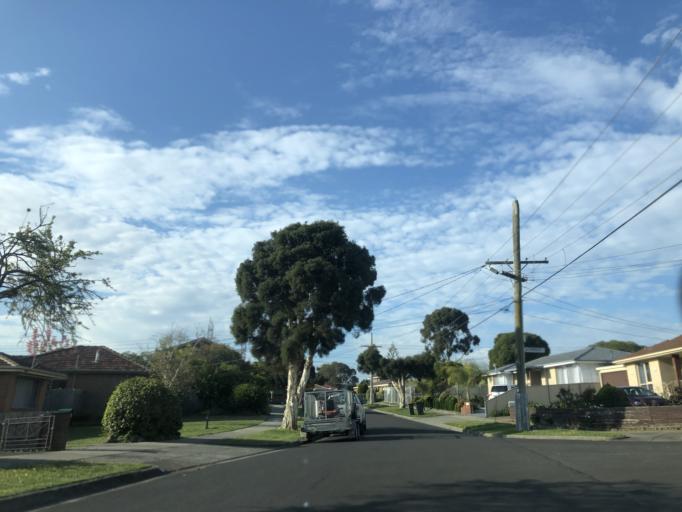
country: AU
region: Victoria
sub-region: Monash
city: Notting Hill
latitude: -37.8967
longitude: 145.1556
